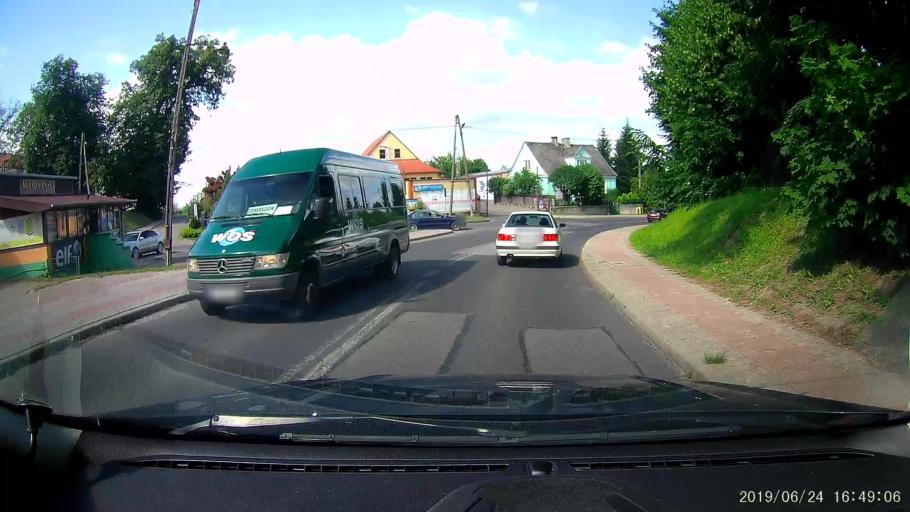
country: PL
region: Lublin Voivodeship
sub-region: Powiat tomaszowski
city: Laszczow
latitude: 50.5328
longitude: 23.7202
